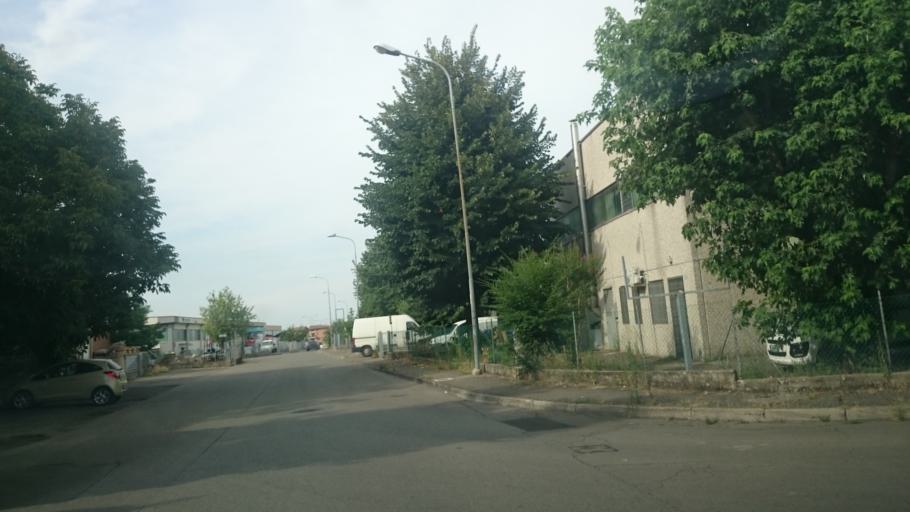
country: IT
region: Emilia-Romagna
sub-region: Provincia di Reggio Emilia
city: Forche
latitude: 44.6687
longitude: 10.5972
